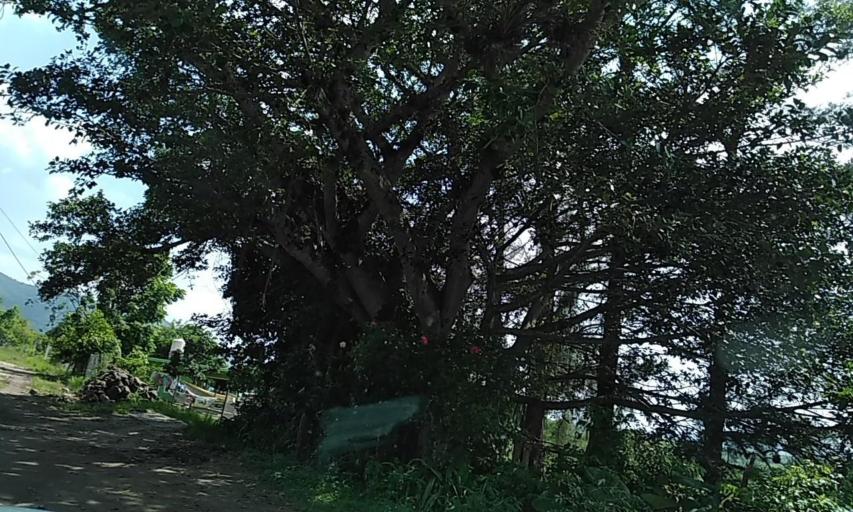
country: MX
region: Veracruz
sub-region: Emiliano Zapata
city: Dos Rios
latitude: 19.4424
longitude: -96.7836
